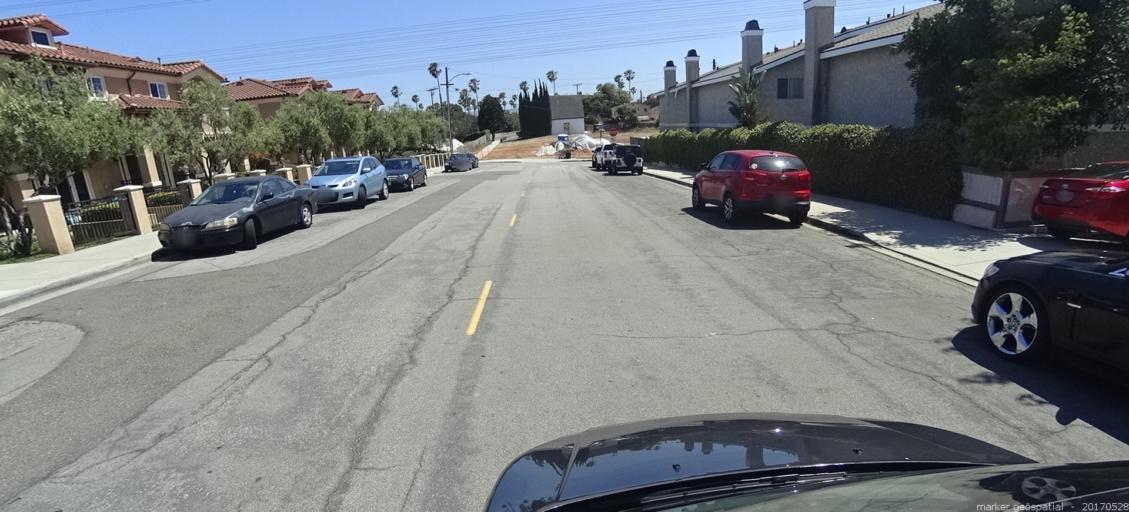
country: US
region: California
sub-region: Los Angeles County
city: Lawndale
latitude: 33.8706
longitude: -118.3600
